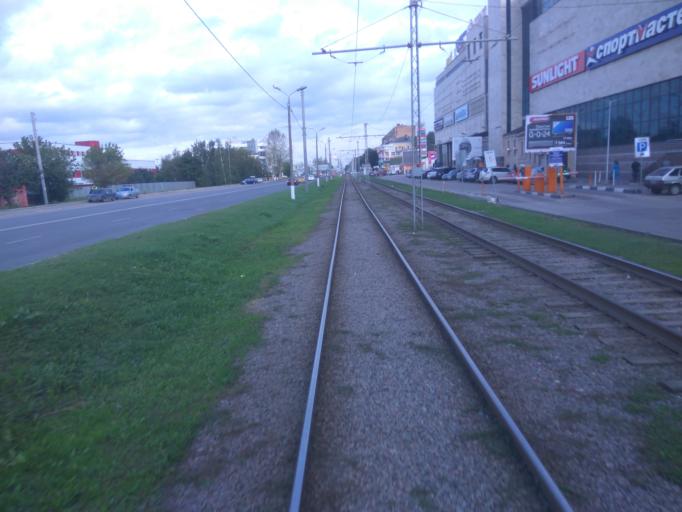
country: RU
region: Moskovskaya
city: Kolomna
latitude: 55.0851
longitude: 38.7994
